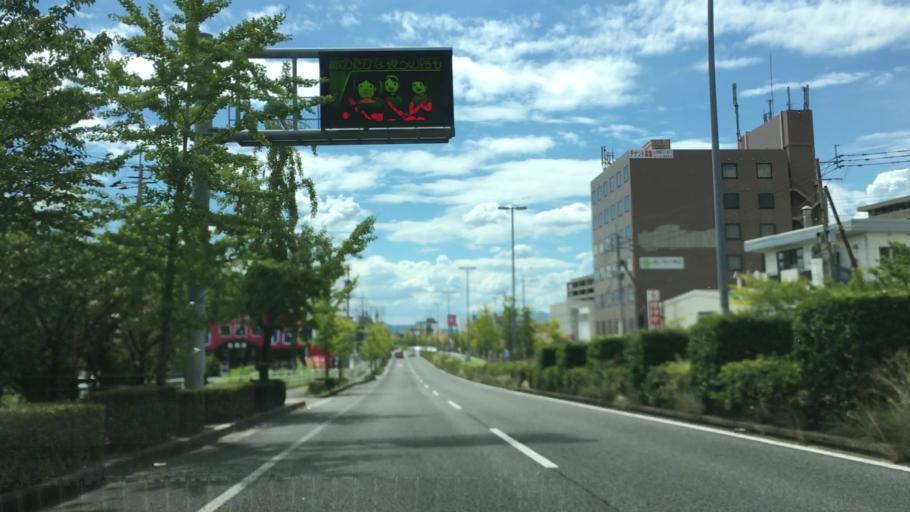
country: JP
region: Saga Prefecture
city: Saga-shi
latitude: 33.2729
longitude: 130.2809
